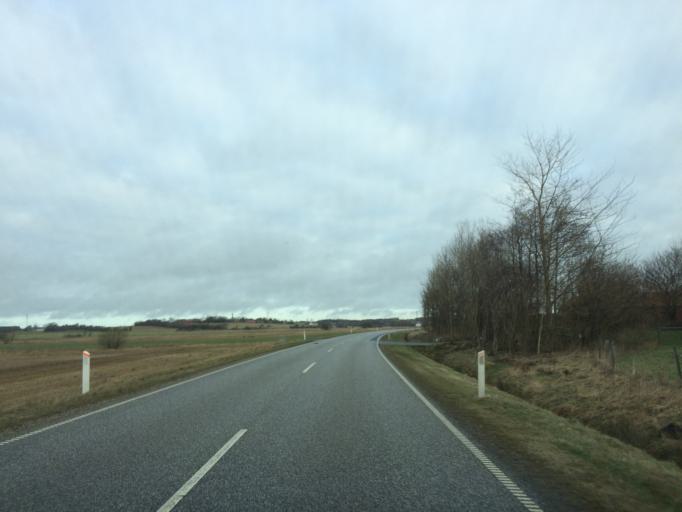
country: DK
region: Central Jutland
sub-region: Struer Kommune
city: Struer
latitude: 56.4061
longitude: 8.4665
